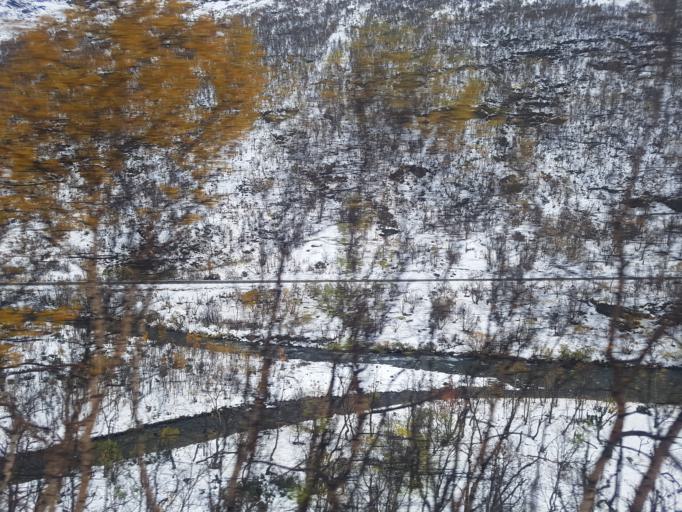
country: NO
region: Sor-Trondelag
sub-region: Oppdal
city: Oppdal
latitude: 62.3371
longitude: 9.6226
